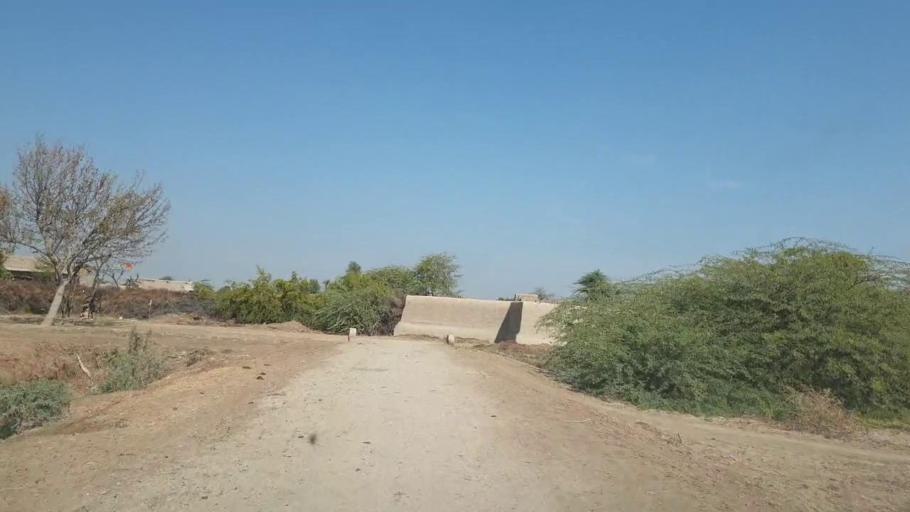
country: PK
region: Sindh
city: Mirpur Khas
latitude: 25.6309
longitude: 69.0954
